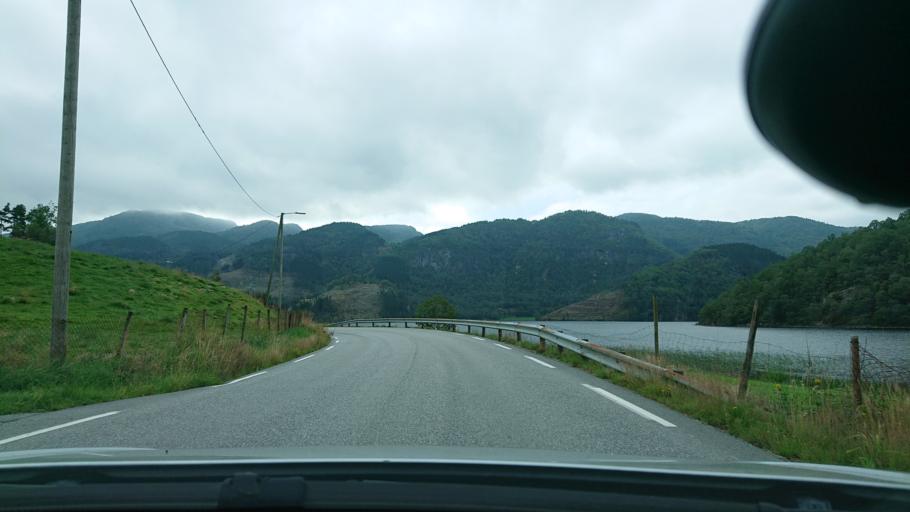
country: NO
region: Rogaland
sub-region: Hjelmeland
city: Hjelmelandsvagen
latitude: 59.2327
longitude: 6.1896
